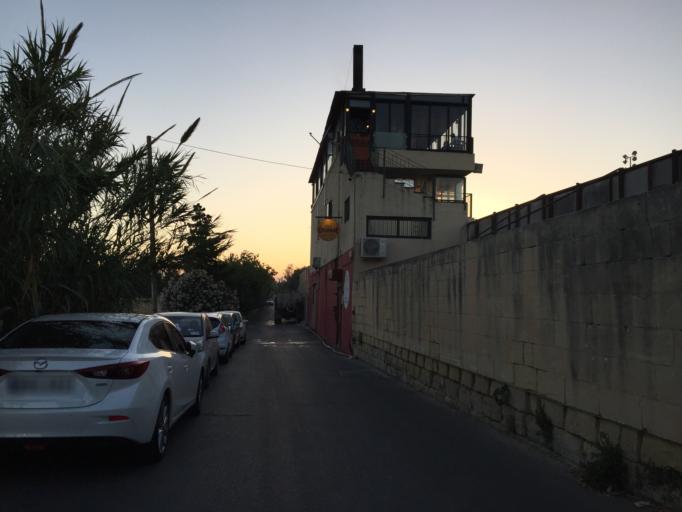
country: MT
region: Il-Hamrun
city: Hamrun
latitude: 35.8771
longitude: 14.4869
